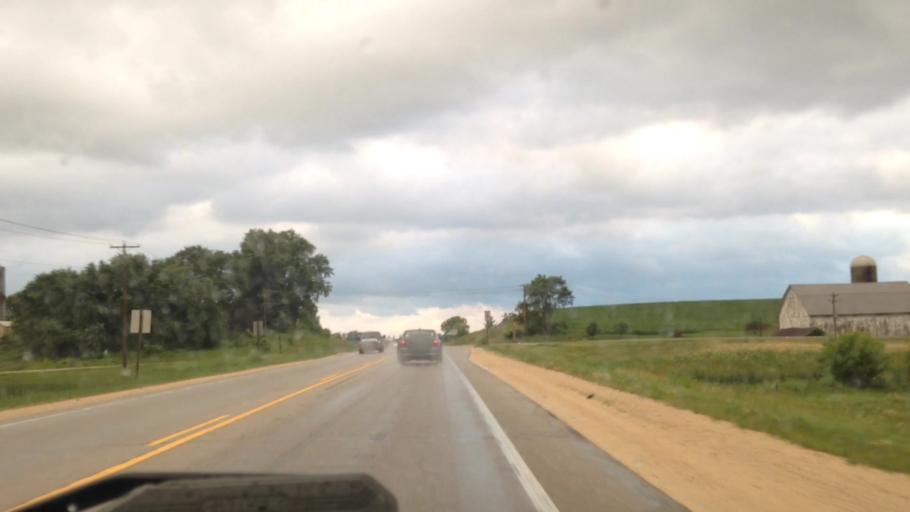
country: US
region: Wisconsin
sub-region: Dodge County
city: Mayville
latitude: 43.4431
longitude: -88.5605
